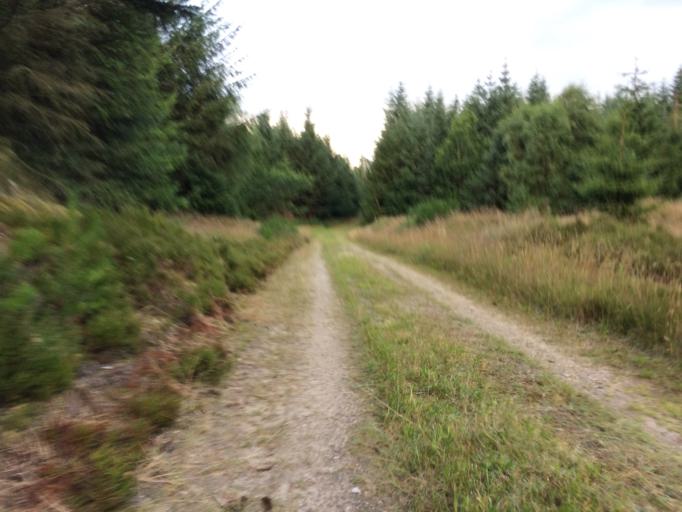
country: DK
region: Central Jutland
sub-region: Holstebro Kommune
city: Ulfborg
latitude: 56.2583
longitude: 8.3790
